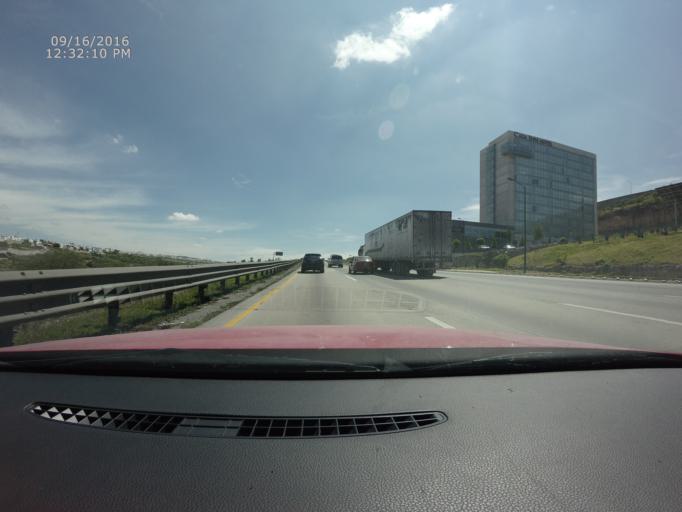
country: MX
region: Queretaro
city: La Canada
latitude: 20.5876
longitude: -100.3481
